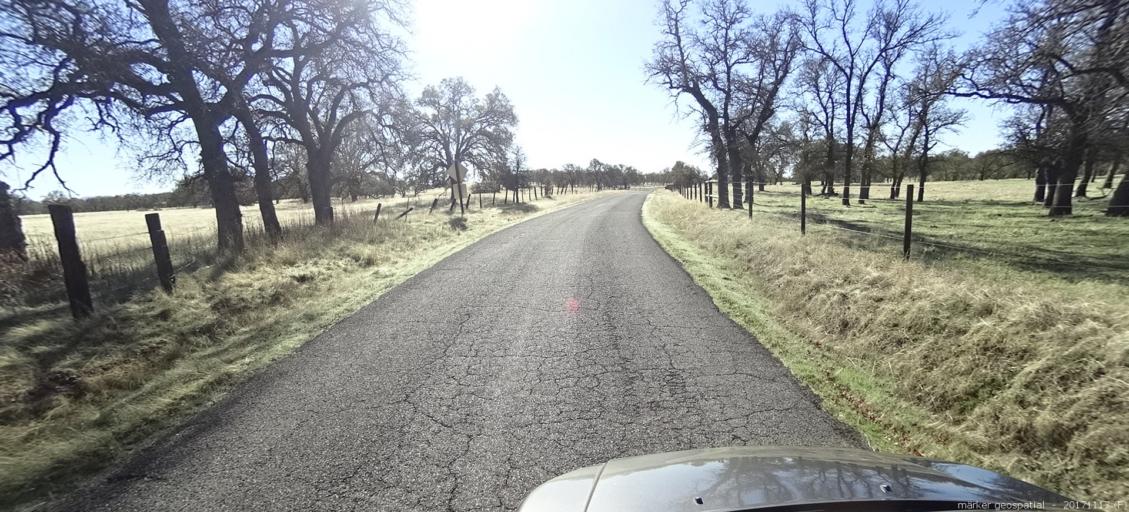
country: US
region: California
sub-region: Shasta County
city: Cottonwood
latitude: 40.4366
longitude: -122.1885
